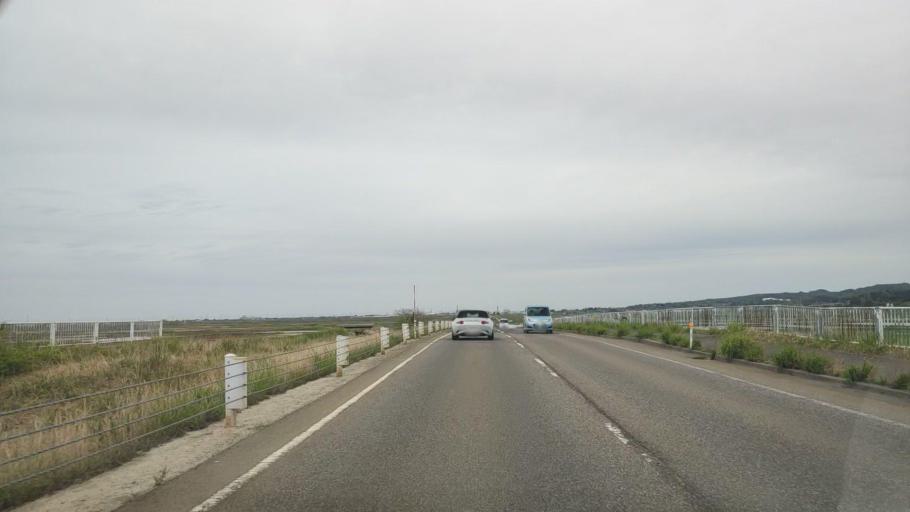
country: JP
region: Niigata
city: Niitsu-honcho
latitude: 37.7583
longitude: 139.0931
